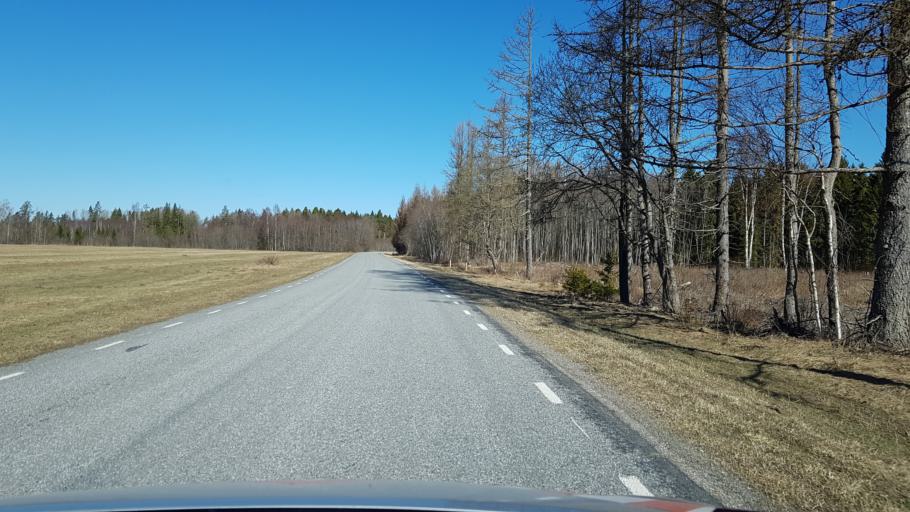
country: EE
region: Laeaene-Virumaa
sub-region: Haljala vald
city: Haljala
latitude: 59.4766
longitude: 26.2496
